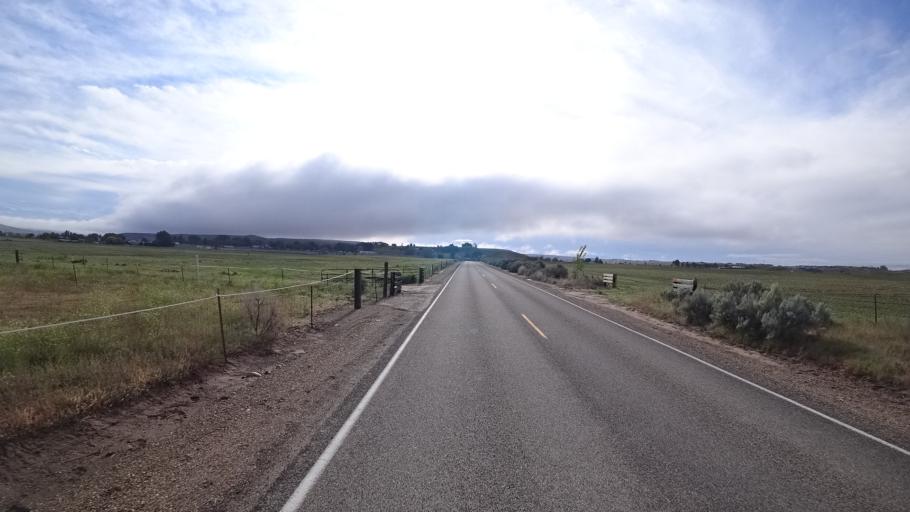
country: US
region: Idaho
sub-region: Ada County
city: Star
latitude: 43.7718
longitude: -116.4783
